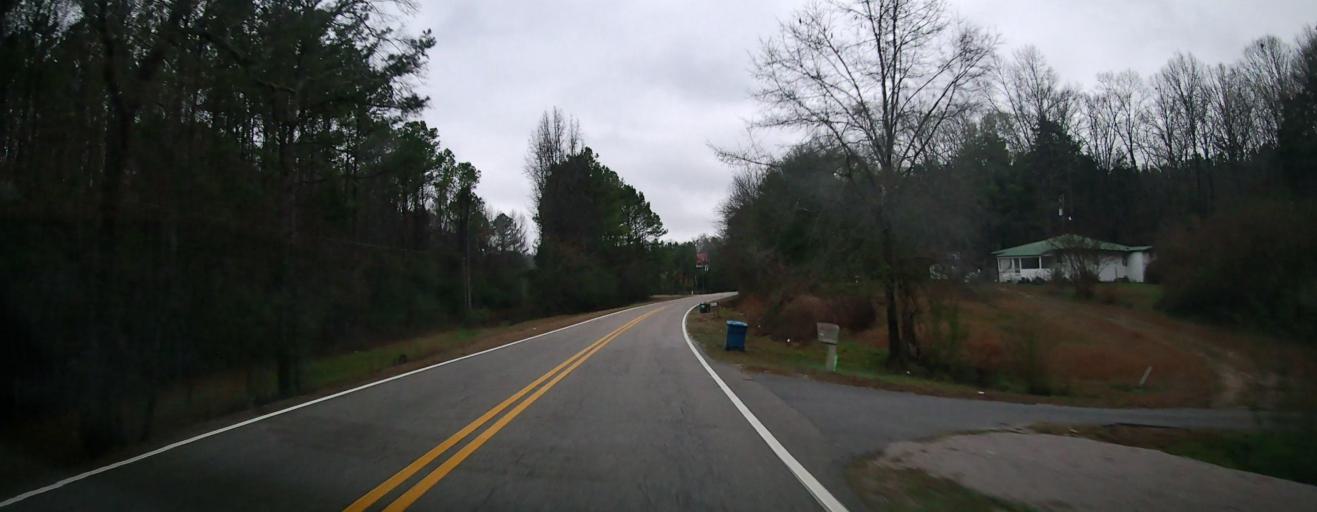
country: US
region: Alabama
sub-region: Bibb County
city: Centreville
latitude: 32.9798
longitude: -87.1463
